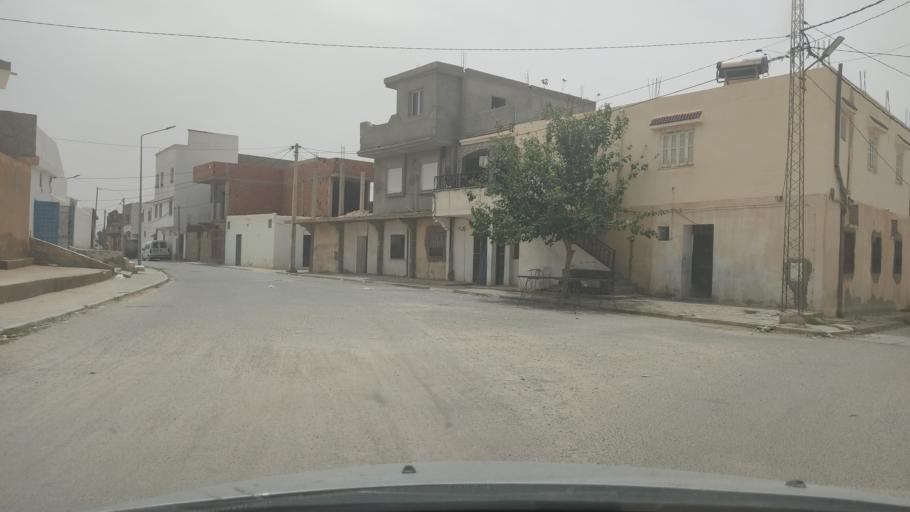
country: TN
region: Gafsa
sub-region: Gafsa Municipality
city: Gafsa
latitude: 34.3335
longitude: 8.9545
